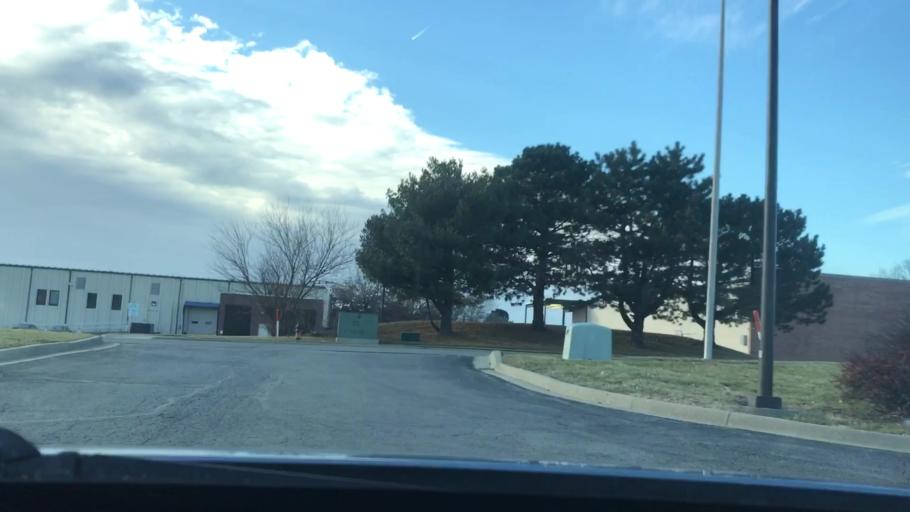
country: US
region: Missouri
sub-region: Platte County
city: Weatherby Lake
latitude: 39.2692
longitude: -94.6691
